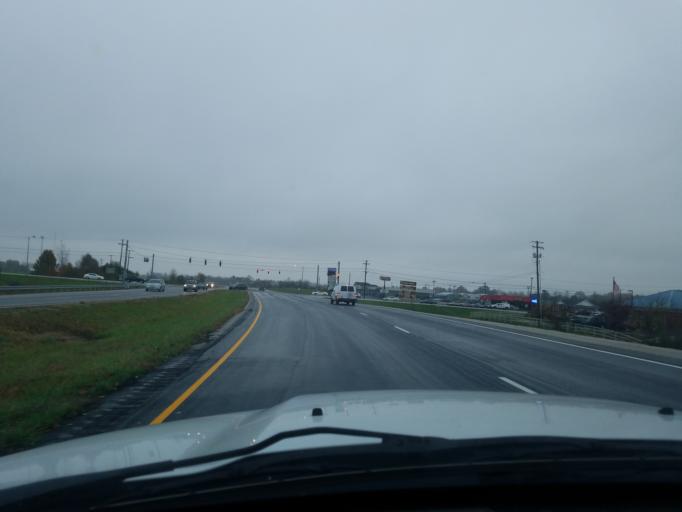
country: US
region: Kentucky
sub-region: Larue County
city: Hodgenville
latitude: 37.5515
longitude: -85.7360
